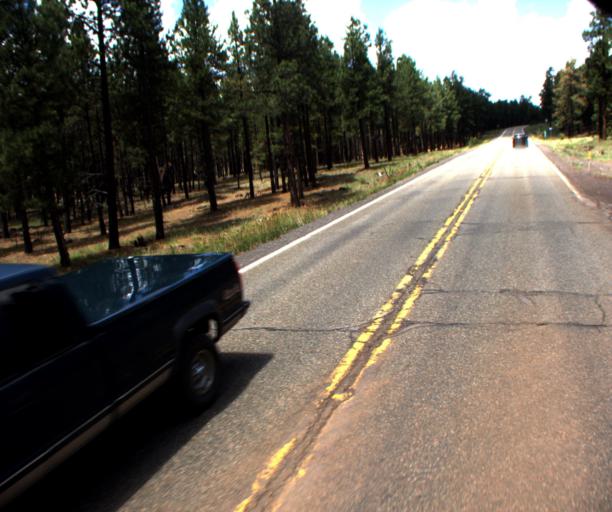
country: US
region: Arizona
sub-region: Coconino County
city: Parks
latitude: 35.3494
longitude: -111.7902
